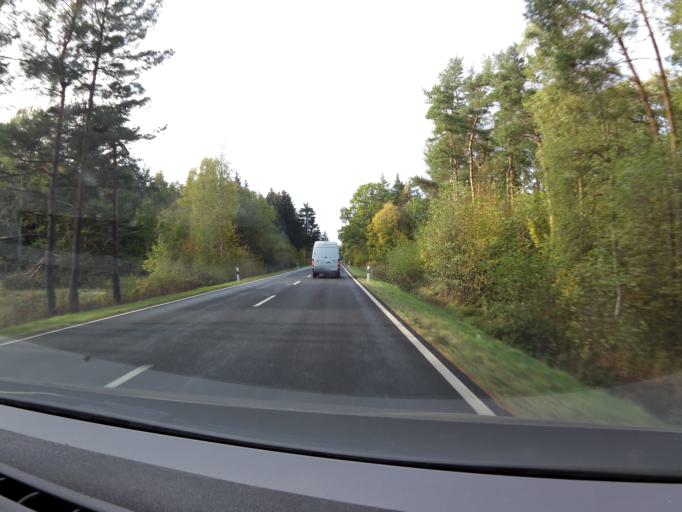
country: DE
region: Thuringia
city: Crawinkel
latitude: 50.7891
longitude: 10.7606
